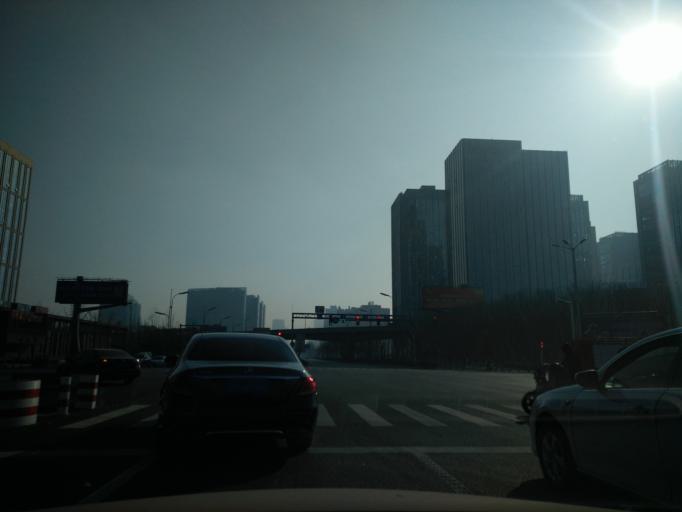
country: CN
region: Beijing
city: Jiugong
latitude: 39.8082
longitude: 116.4905
